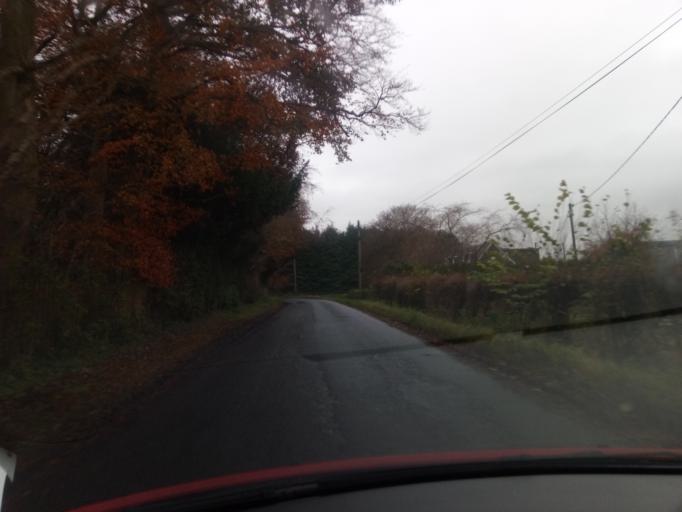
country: GB
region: Scotland
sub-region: The Scottish Borders
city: Newtown St Boswells
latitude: 55.5540
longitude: -2.6861
